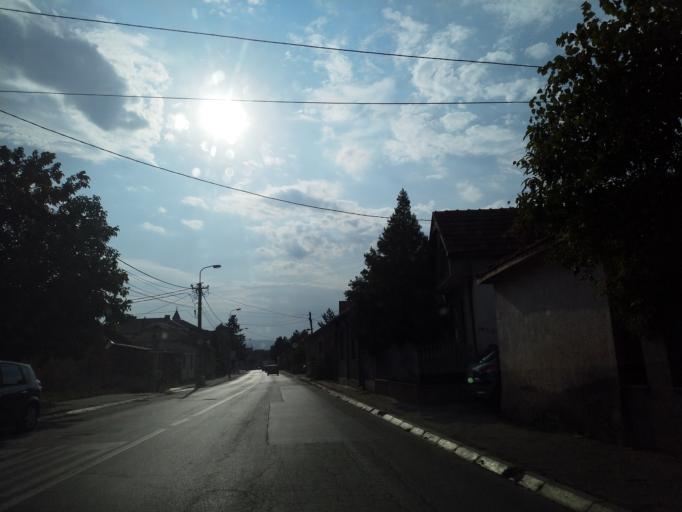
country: RS
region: Central Serbia
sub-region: Pomoravski Okrug
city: Paracin
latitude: 43.8652
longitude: 21.4168
